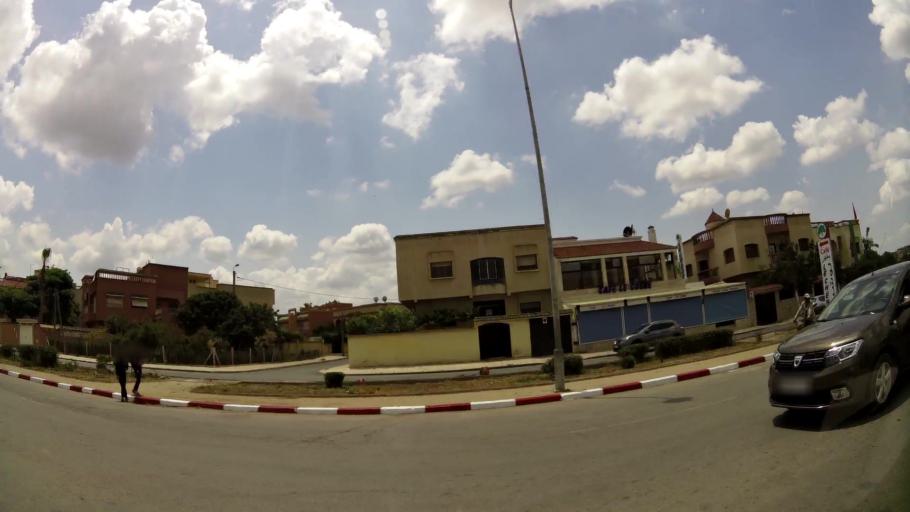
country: MA
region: Rabat-Sale-Zemmour-Zaer
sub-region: Khemisset
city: Tiflet
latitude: 34.0100
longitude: -6.5277
